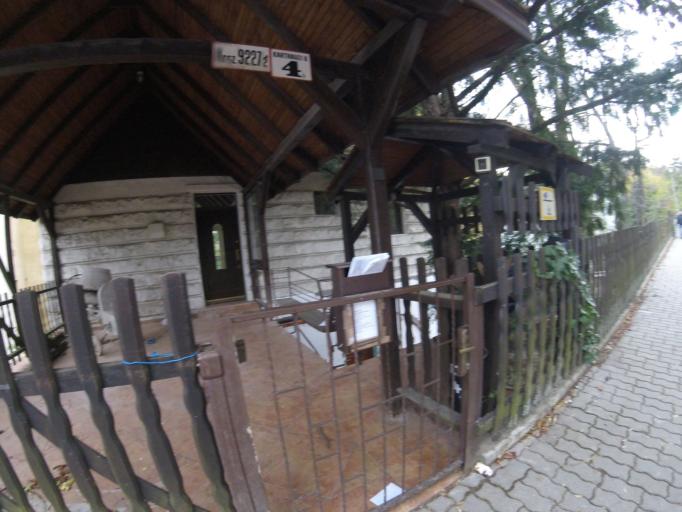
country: HU
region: Budapest
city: Budapest XII. keruelet
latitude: 47.4965
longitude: 18.9883
